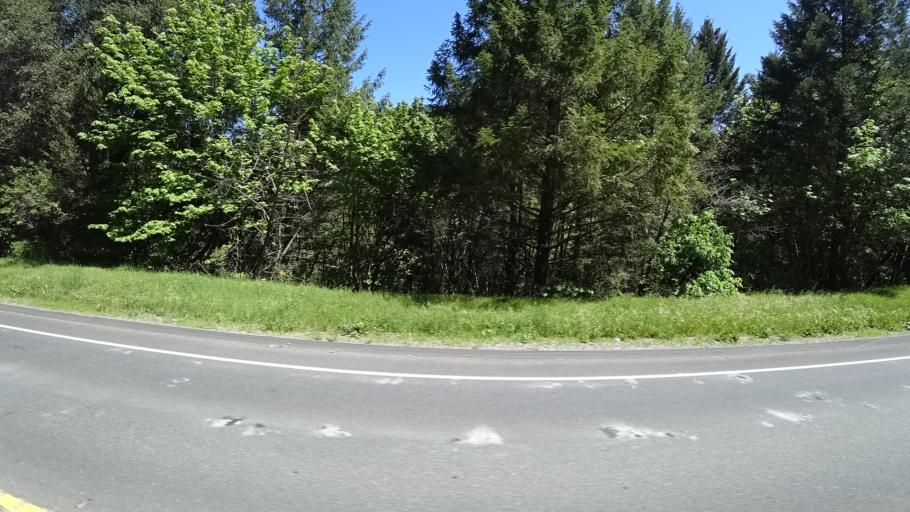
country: US
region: California
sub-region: Humboldt County
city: Willow Creek
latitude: 40.9294
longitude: -123.6258
